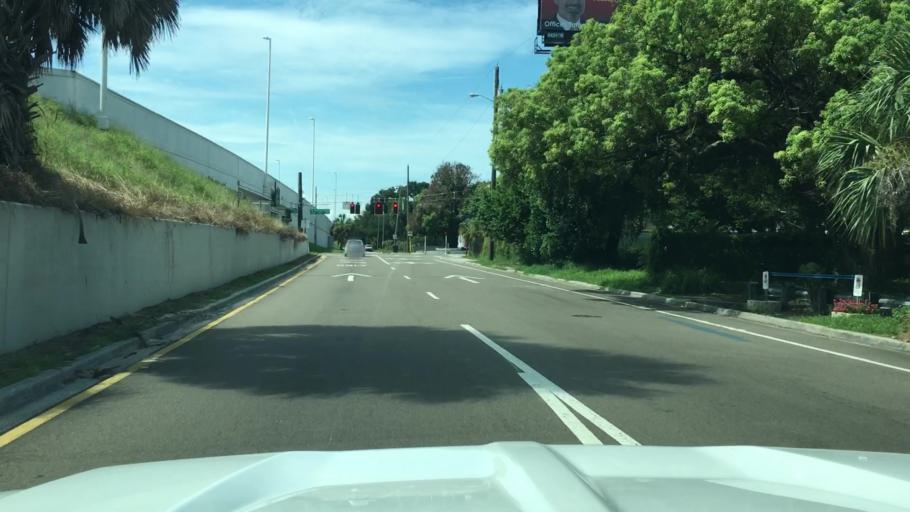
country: US
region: Florida
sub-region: Hillsborough County
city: Tampa
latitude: 27.9717
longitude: -82.4539
